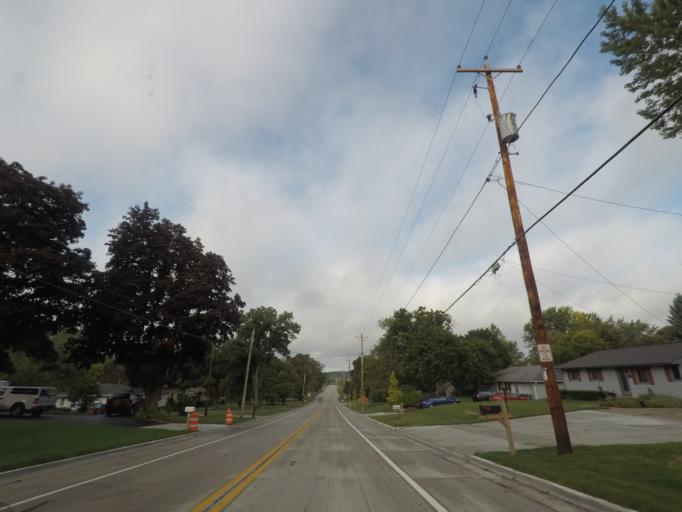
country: US
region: Wisconsin
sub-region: Waukesha County
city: Waukesha
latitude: 43.0321
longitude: -88.2636
